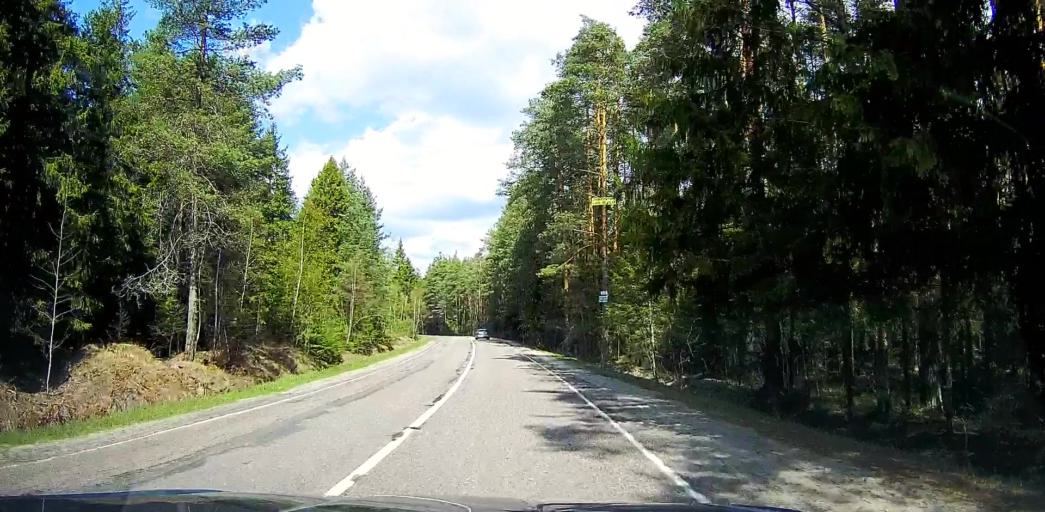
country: RU
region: Moskovskaya
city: Davydovo
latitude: 55.5666
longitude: 38.8207
